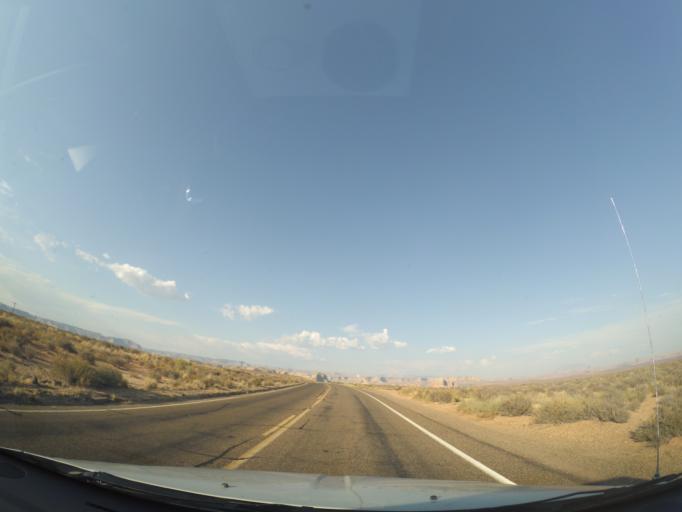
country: US
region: Arizona
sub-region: Coconino County
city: Page
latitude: 36.9867
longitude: -111.5215
